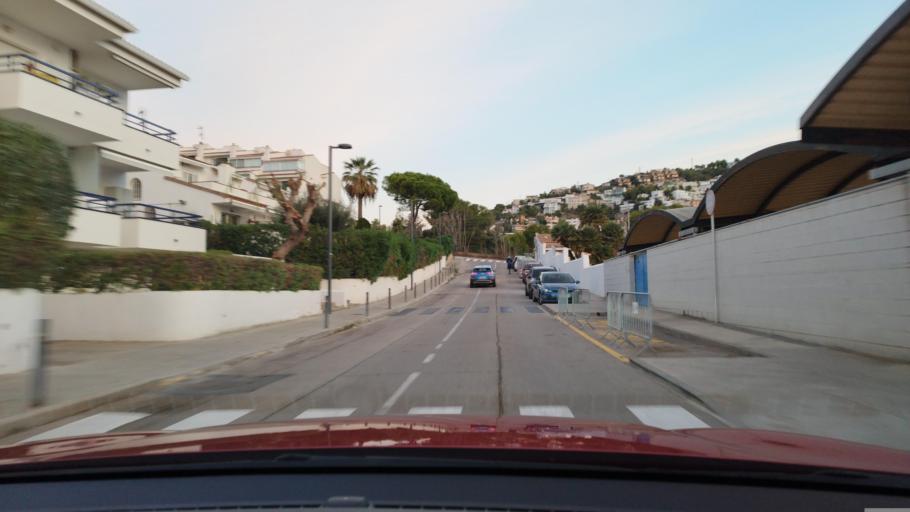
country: ES
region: Catalonia
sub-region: Provincia de Barcelona
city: Sitges
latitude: 41.2367
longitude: 1.8257
